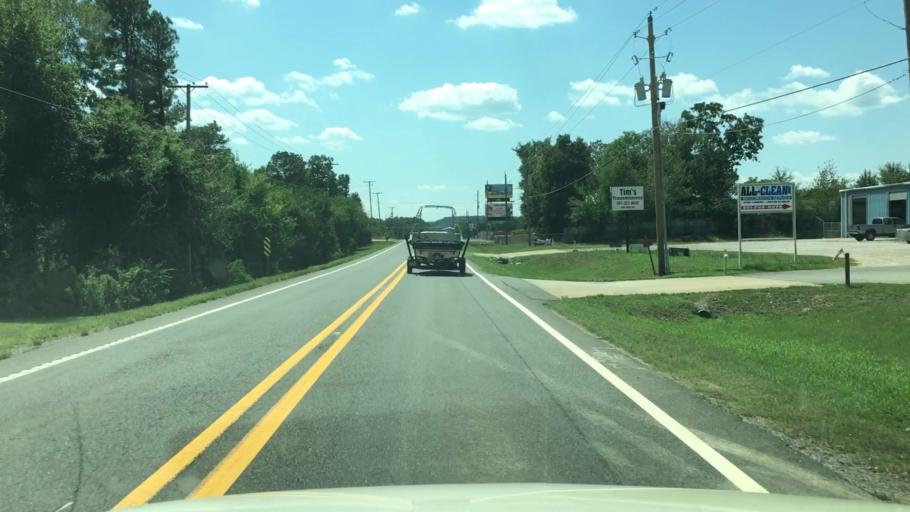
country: US
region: Arkansas
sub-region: Garland County
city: Piney
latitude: 34.5105
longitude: -93.2139
